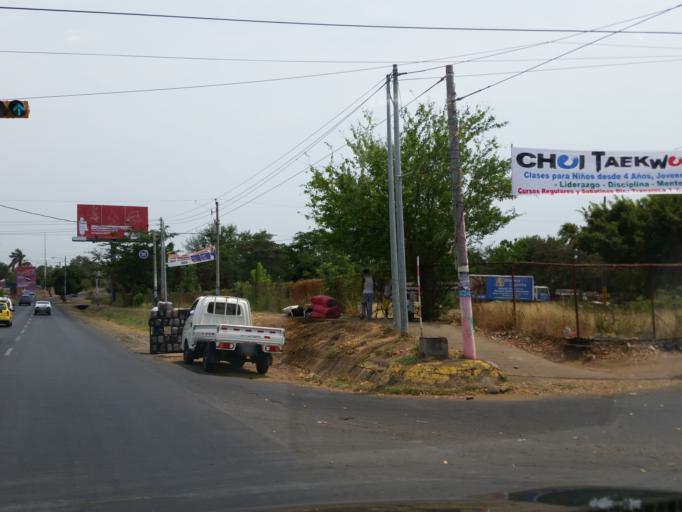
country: NI
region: Managua
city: Managua
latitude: 12.1345
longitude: -86.2680
